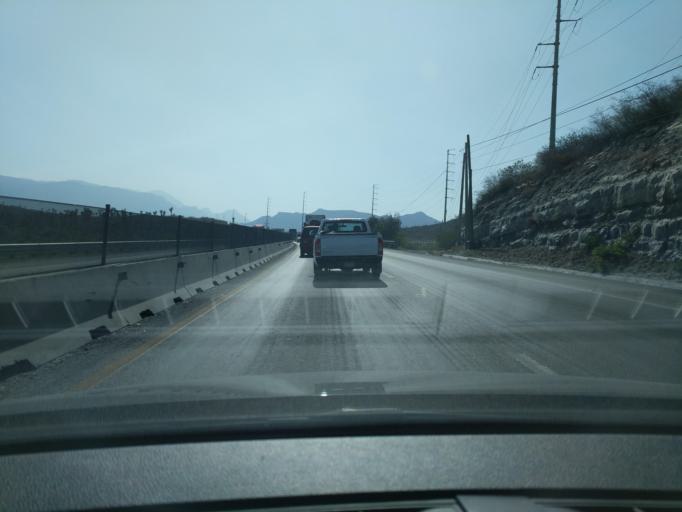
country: MX
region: Nuevo Leon
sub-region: Garcia
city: Los Parques
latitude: 25.7526
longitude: -100.5051
